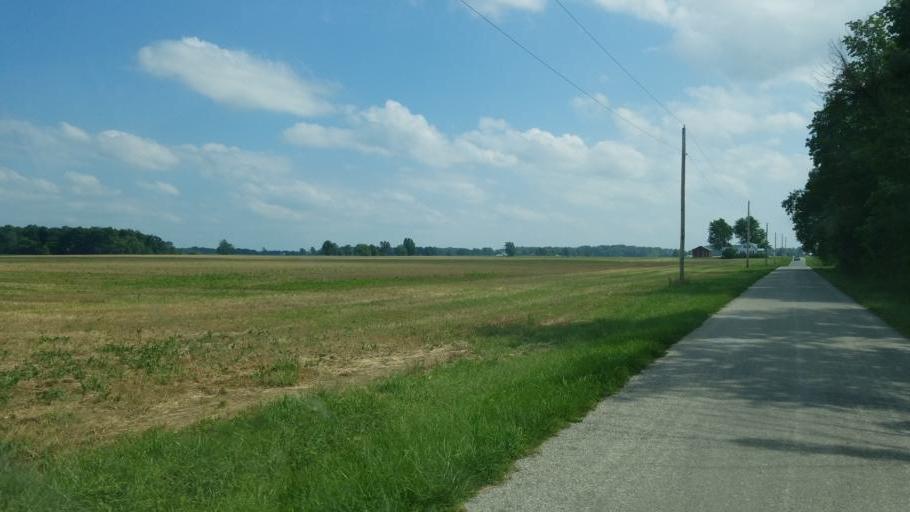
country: US
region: Ohio
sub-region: Huron County
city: Willard
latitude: 40.9747
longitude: -82.7623
